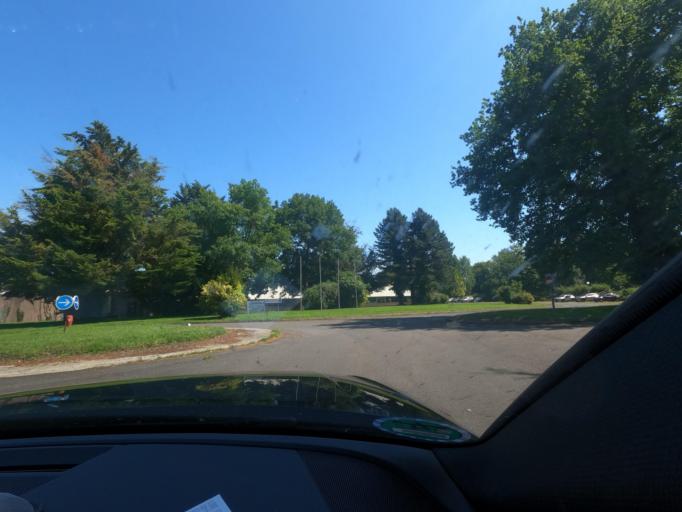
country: FR
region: Lower Normandy
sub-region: Departement du Calvados
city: La Riviere-Saint-Sauveur
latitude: 49.3946
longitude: 0.2585
